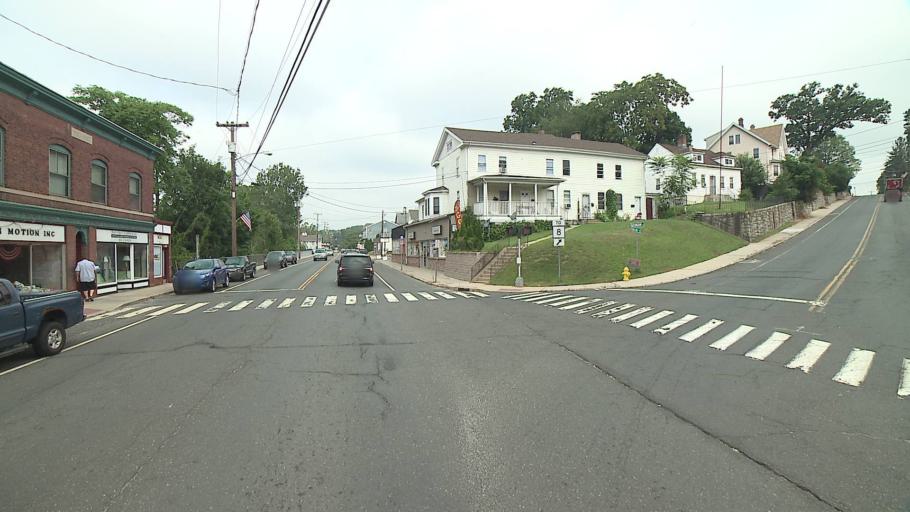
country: US
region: Connecticut
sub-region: Litchfield County
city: Oakville
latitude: 41.5872
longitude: -73.0844
